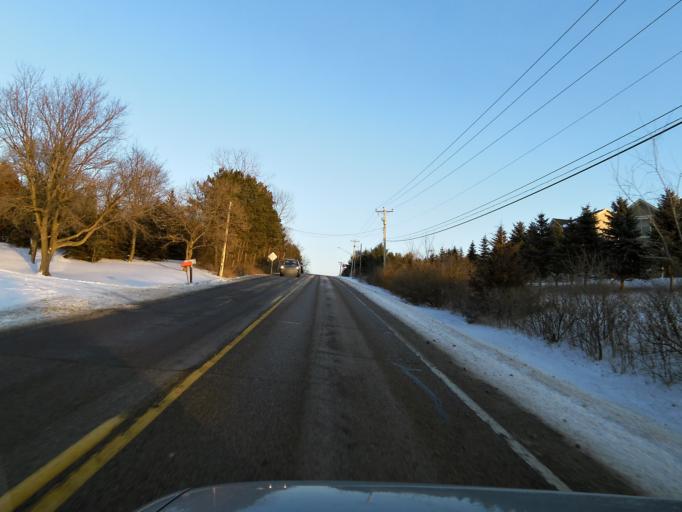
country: US
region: Minnesota
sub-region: Washington County
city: Woodbury
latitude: 44.9199
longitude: -92.8847
